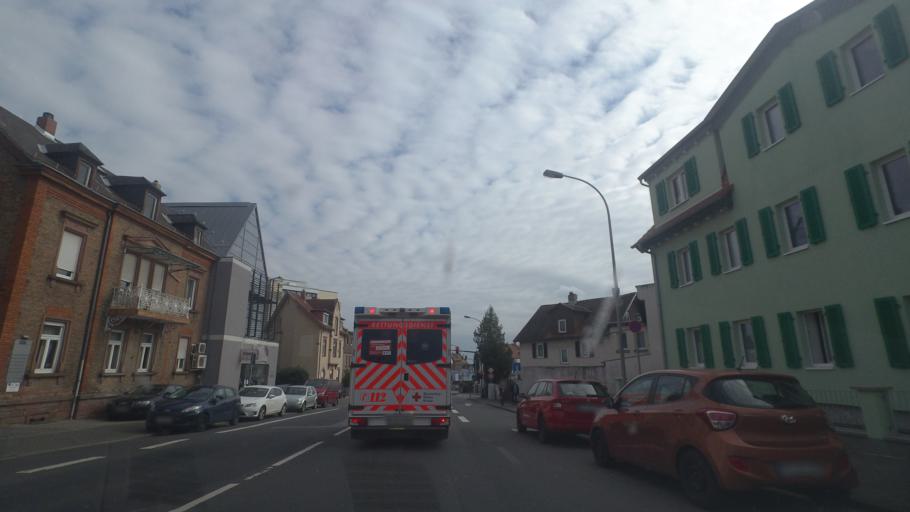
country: DE
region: Hesse
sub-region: Regierungsbezirk Darmstadt
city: Bad Vilbel
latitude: 50.1555
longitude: 8.7476
